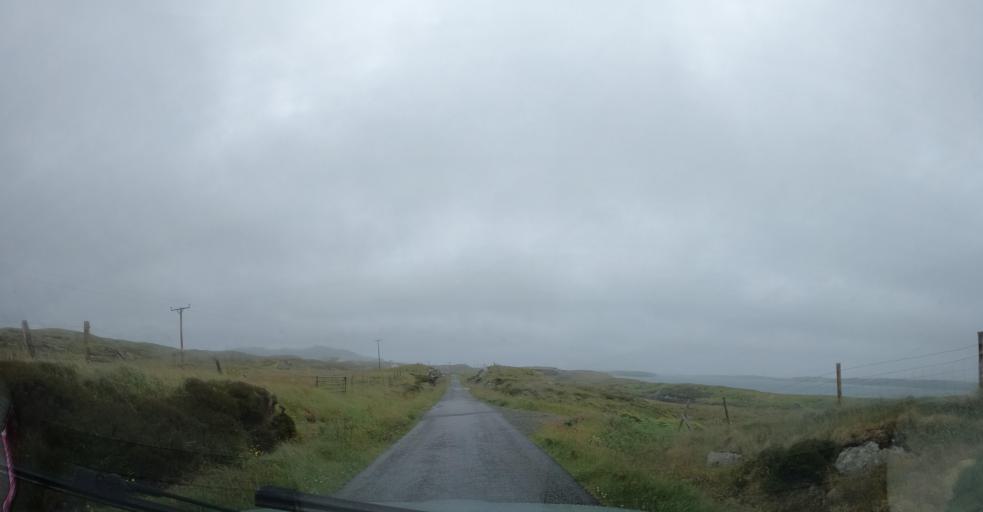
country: GB
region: Scotland
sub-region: Eilean Siar
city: Benbecula
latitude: 57.4801
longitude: -7.2249
